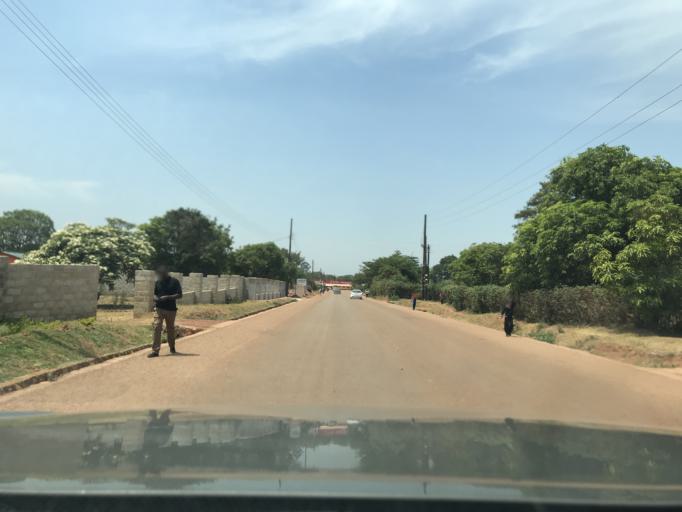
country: ZM
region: Northern
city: Kasama
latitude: -10.2031
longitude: 31.1854
